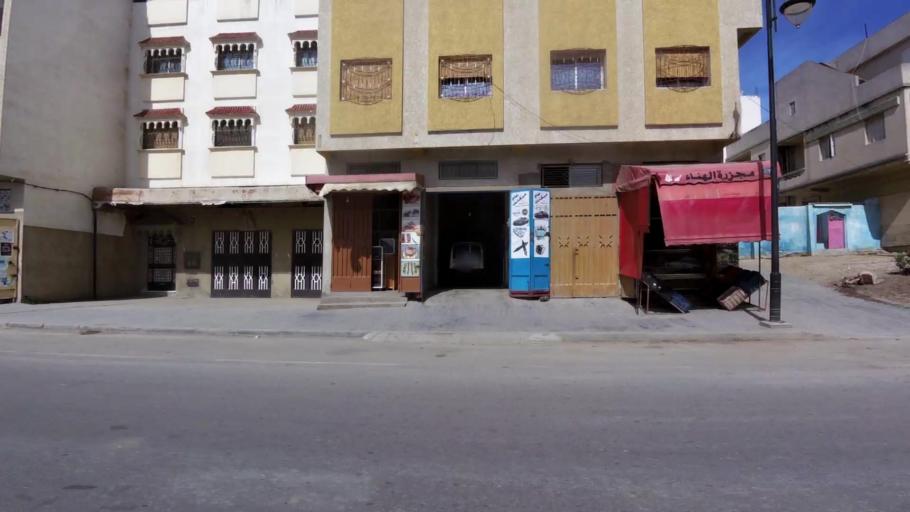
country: MA
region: Tanger-Tetouan
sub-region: Tanger-Assilah
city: Tangier
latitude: 35.7269
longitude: -5.8037
